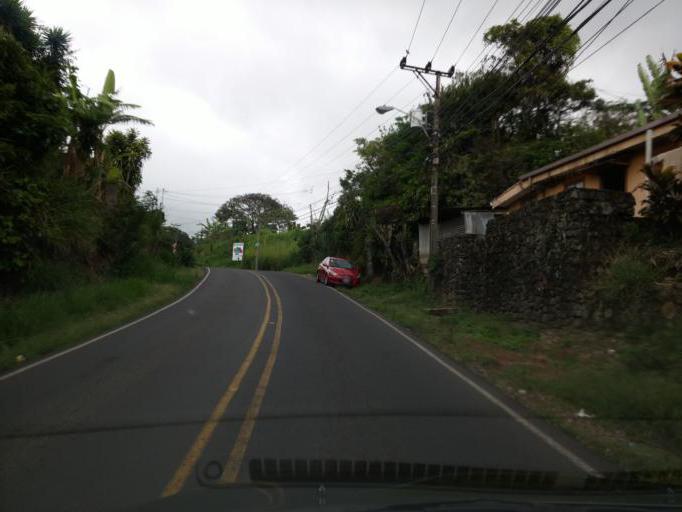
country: CR
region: Heredia
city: Mercedes
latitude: 10.0252
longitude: -84.1237
